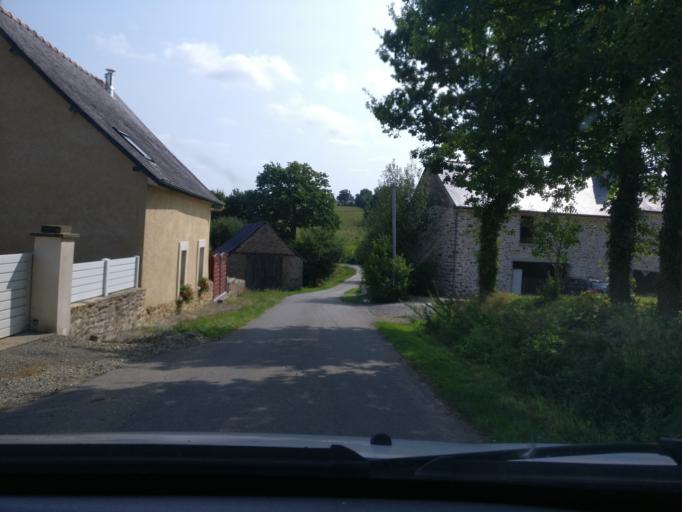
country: FR
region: Brittany
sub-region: Departement d'Ille-et-Vilaine
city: Gosne
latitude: 48.2579
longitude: -1.4795
